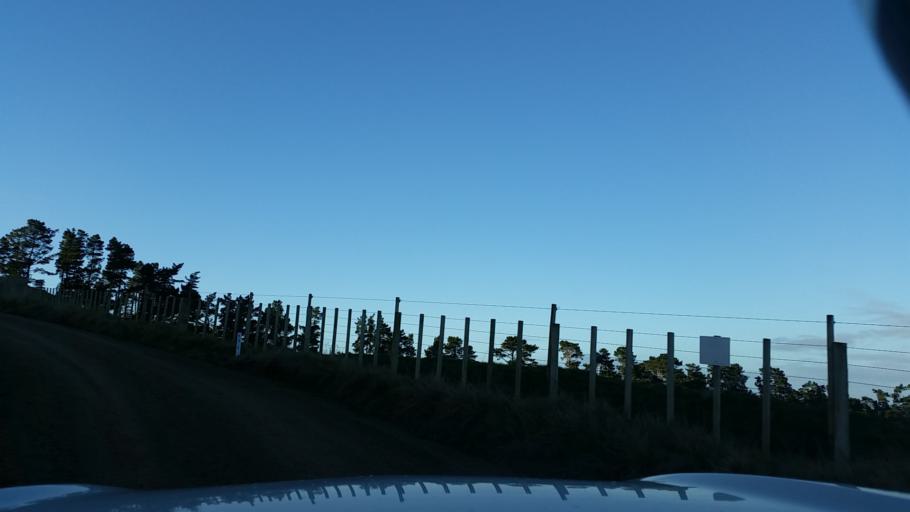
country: NZ
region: Taranaki
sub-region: South Taranaki District
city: Patea
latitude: -39.7556
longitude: 174.7470
